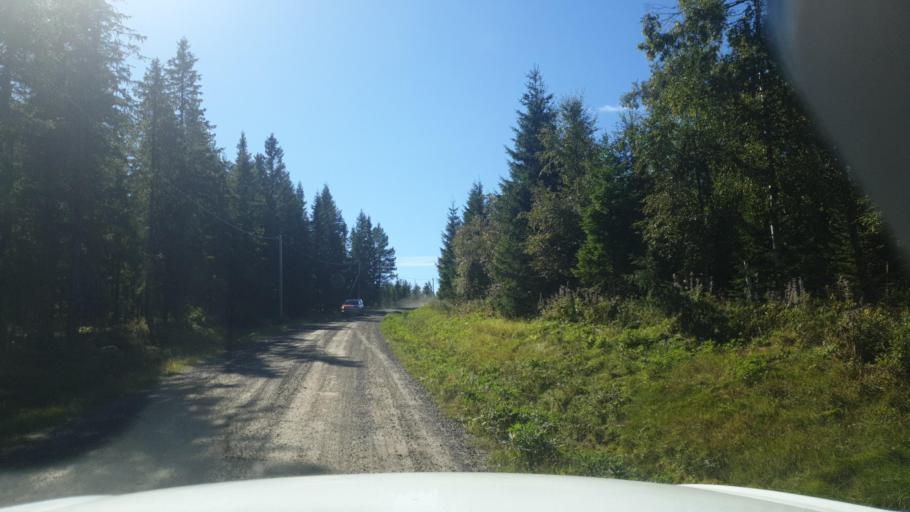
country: SE
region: Vaermland
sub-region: Torsby Kommun
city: Torsby
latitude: 60.1740
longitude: 12.6459
